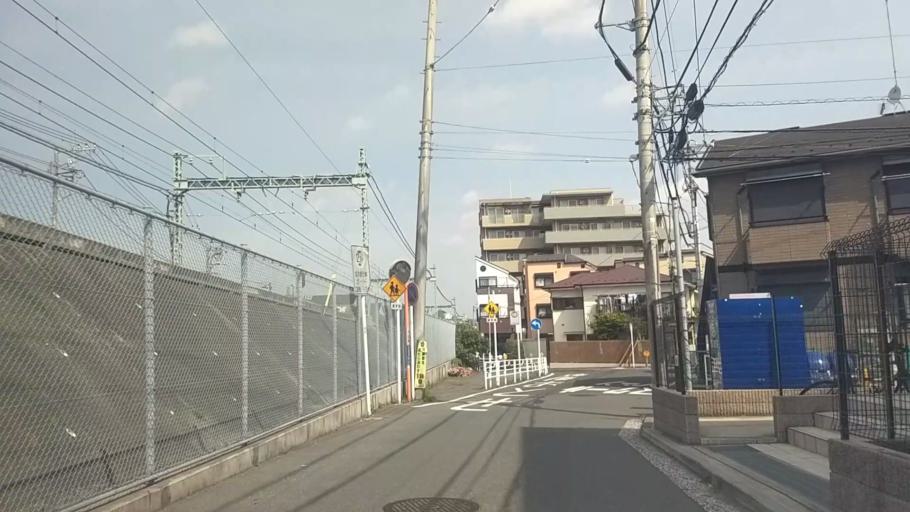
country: JP
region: Kanagawa
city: Yokohama
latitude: 35.3803
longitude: 139.6177
